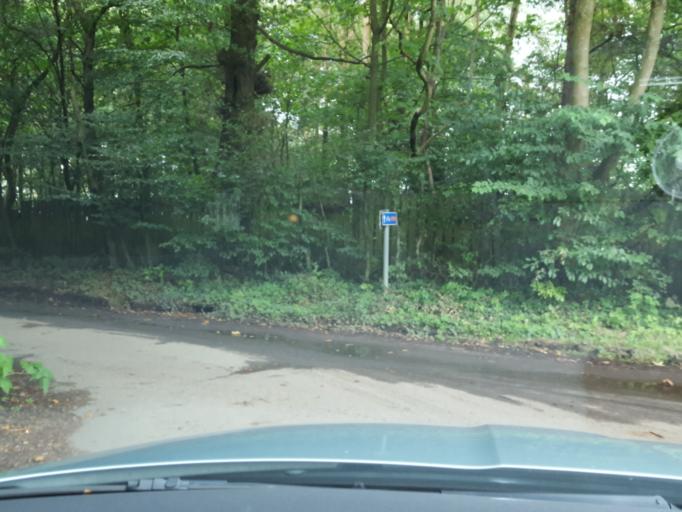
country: GB
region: Scotland
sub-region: West Lothian
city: East Calder
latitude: 55.9116
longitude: -3.4554
